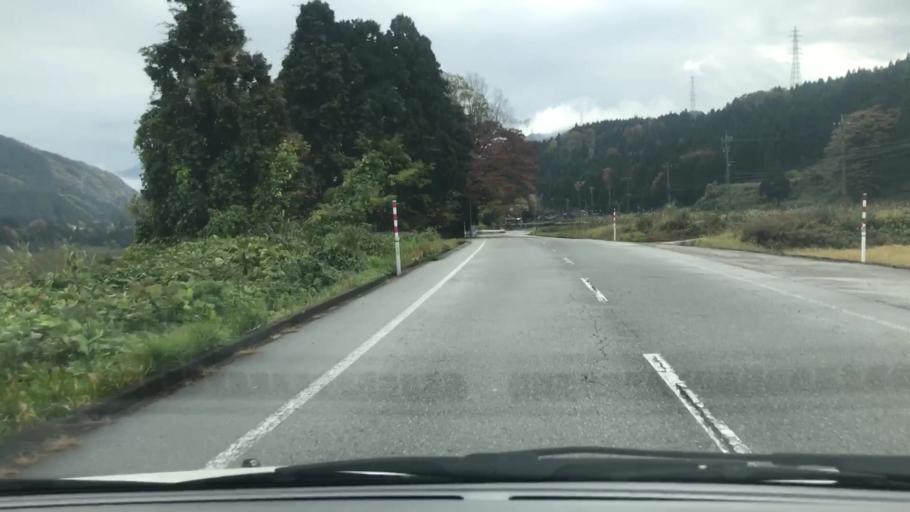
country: JP
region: Toyama
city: Kamiichi
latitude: 36.5877
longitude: 137.3211
